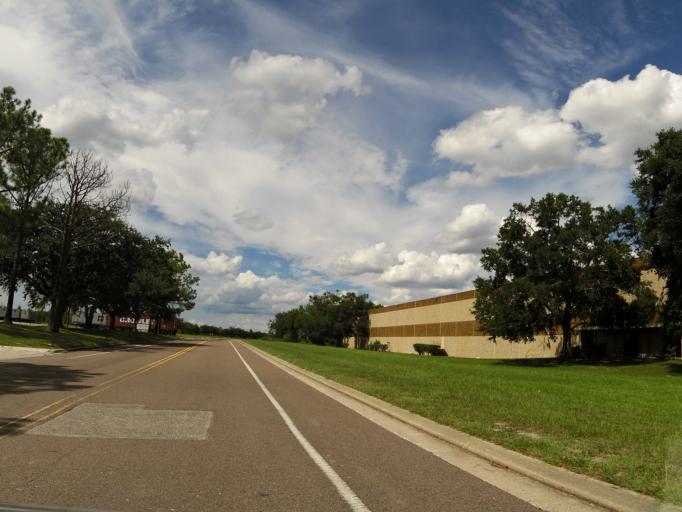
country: US
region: Florida
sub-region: Duval County
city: Jacksonville
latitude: 30.4105
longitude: -81.6432
